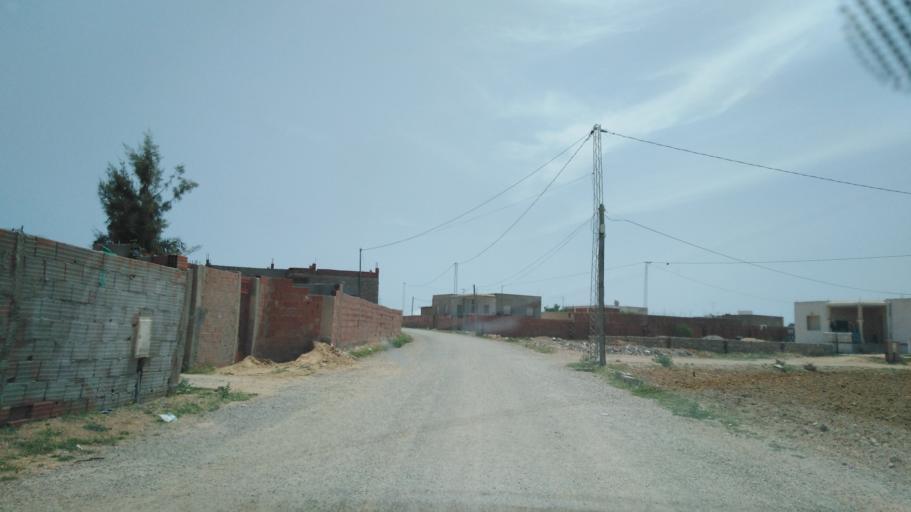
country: TN
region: Safaqis
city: Sfax
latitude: 34.7277
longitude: 10.5537
